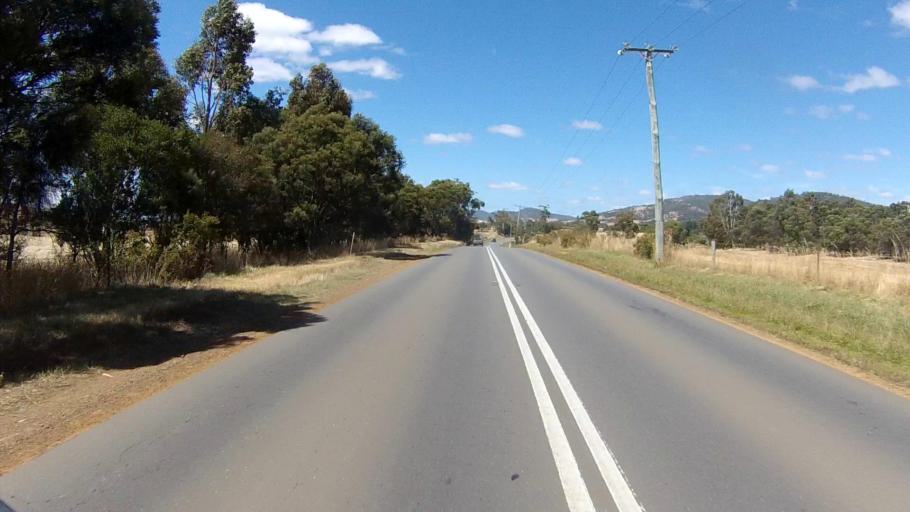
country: AU
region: Tasmania
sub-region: Clarence
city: Cambridge
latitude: -42.7651
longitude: 147.4151
